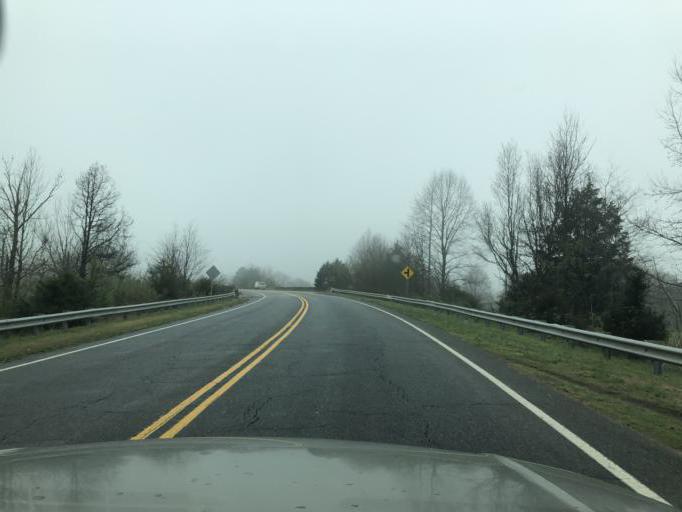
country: US
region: North Carolina
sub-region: Gaston County
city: Cherryville
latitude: 35.3581
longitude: -81.4370
